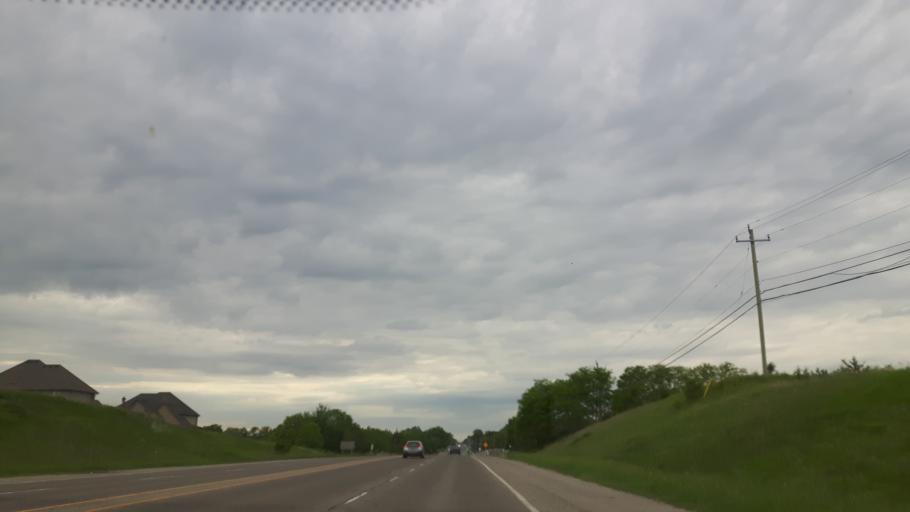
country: CA
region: Ontario
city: London
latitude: 43.0428
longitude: -81.2909
